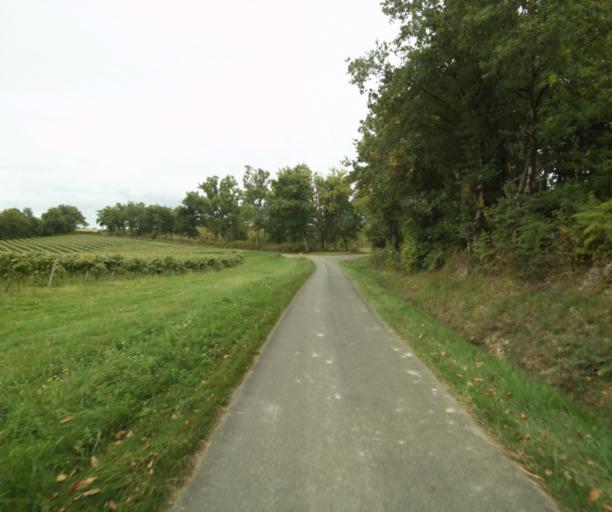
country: FR
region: Midi-Pyrenees
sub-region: Departement du Gers
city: Eauze
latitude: 43.9057
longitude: 0.1202
